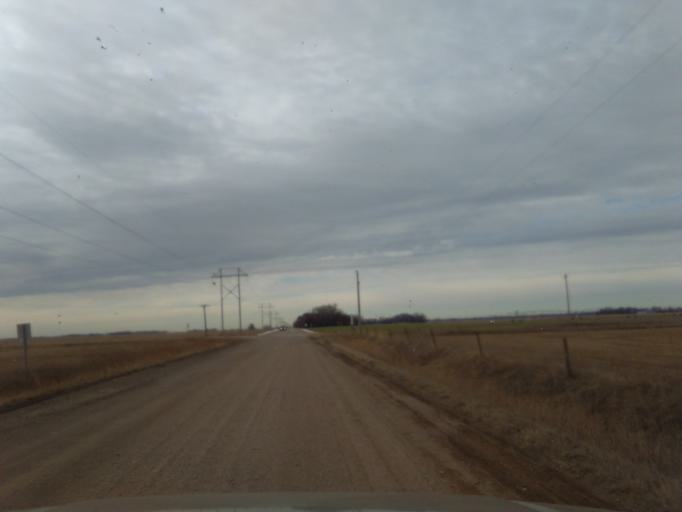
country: US
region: Nebraska
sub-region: Buffalo County
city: Gibbon
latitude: 40.6550
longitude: -98.7992
